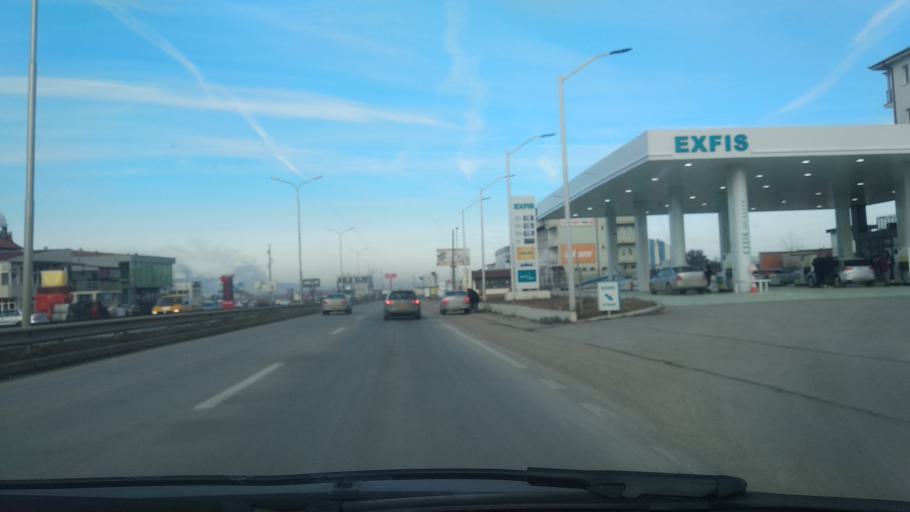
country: XK
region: Pristina
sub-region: Komuna e Prishtines
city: Pristina
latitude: 42.6591
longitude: 21.1349
